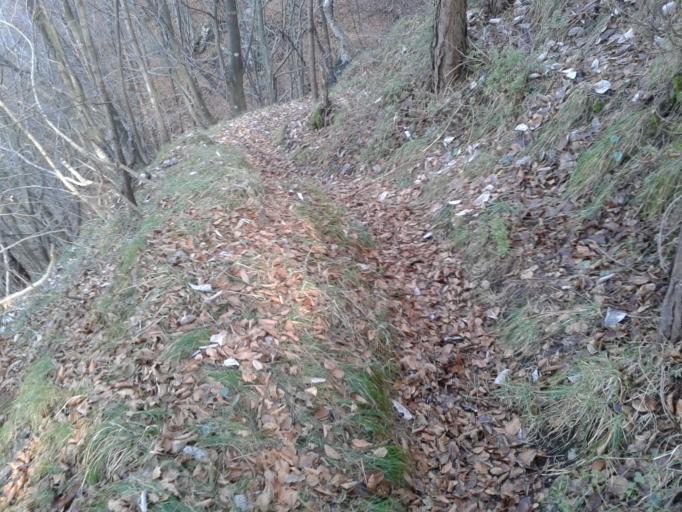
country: IT
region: Trentino-Alto Adige
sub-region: Provincia di Trento
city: Storo
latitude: 45.8353
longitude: 10.5714
